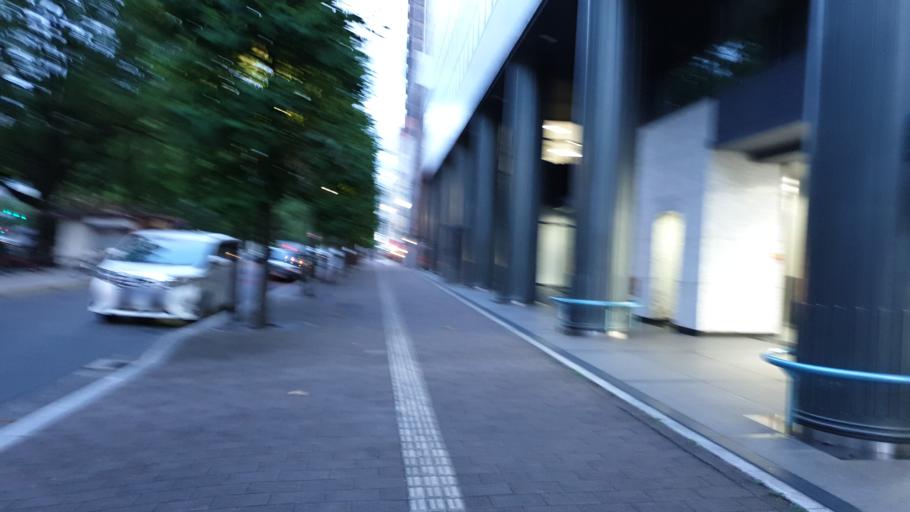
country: JP
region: Hiroshima
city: Hiroshima-shi
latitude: 34.3884
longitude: 132.4592
